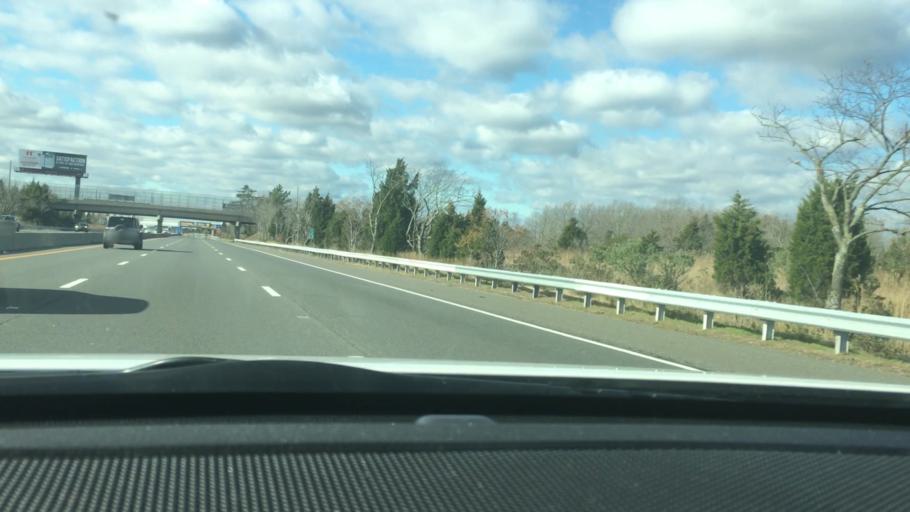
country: US
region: New Jersey
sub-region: Atlantic County
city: Ventnor City
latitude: 39.3749
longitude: -74.4767
